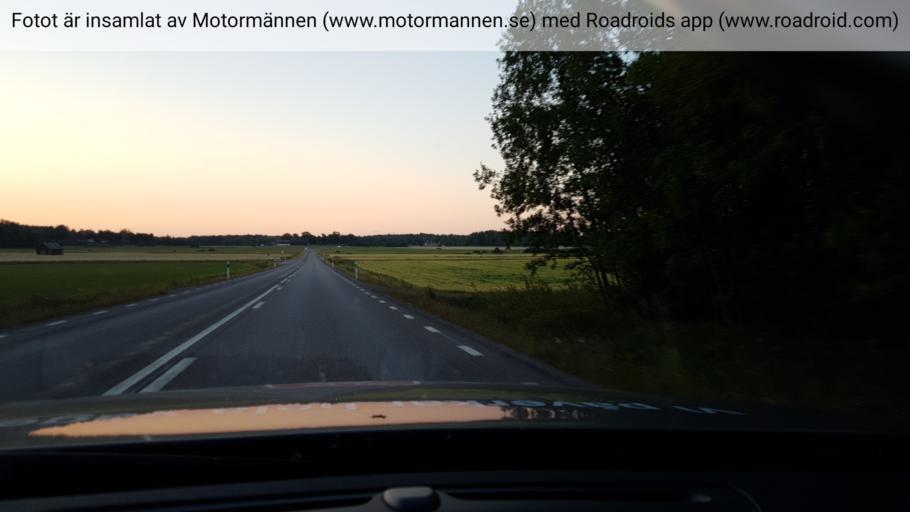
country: SE
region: Uppsala
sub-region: Heby Kommun
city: OEstervala
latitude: 60.0879
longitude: 17.1899
